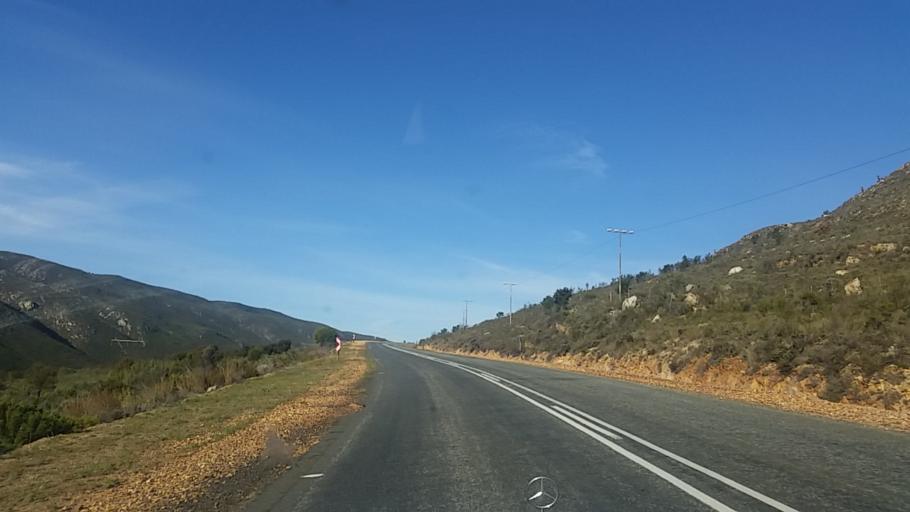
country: ZA
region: Western Cape
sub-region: Eden District Municipality
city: Knysna
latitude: -33.7500
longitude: 22.9676
